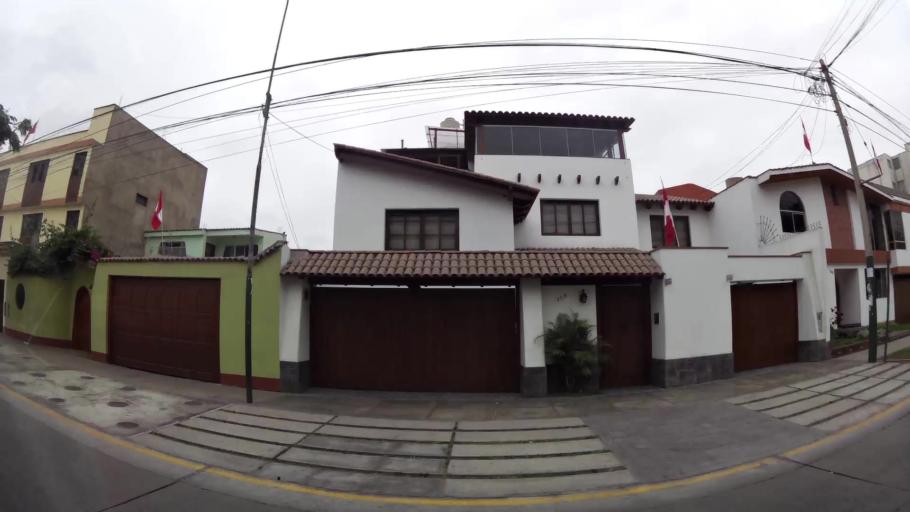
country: PE
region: Lima
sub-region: Lima
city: Surco
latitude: -12.1430
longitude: -76.9977
